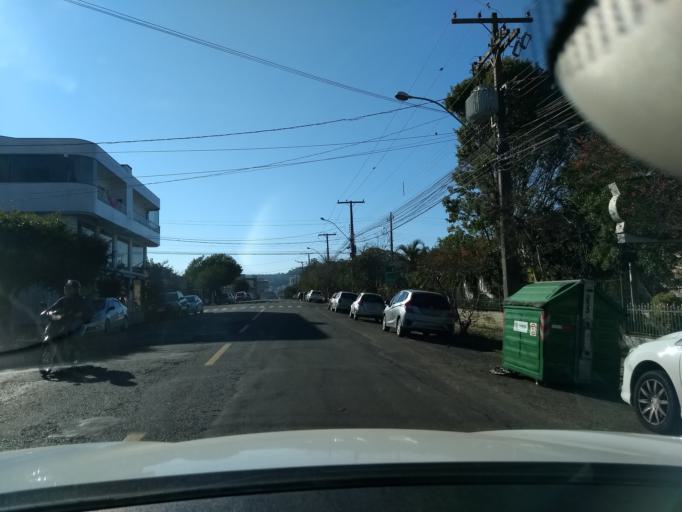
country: BR
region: Rio Grande do Sul
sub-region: Santa Cruz Do Sul
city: Santa Cruz do Sul
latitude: -29.7160
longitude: -52.4387
